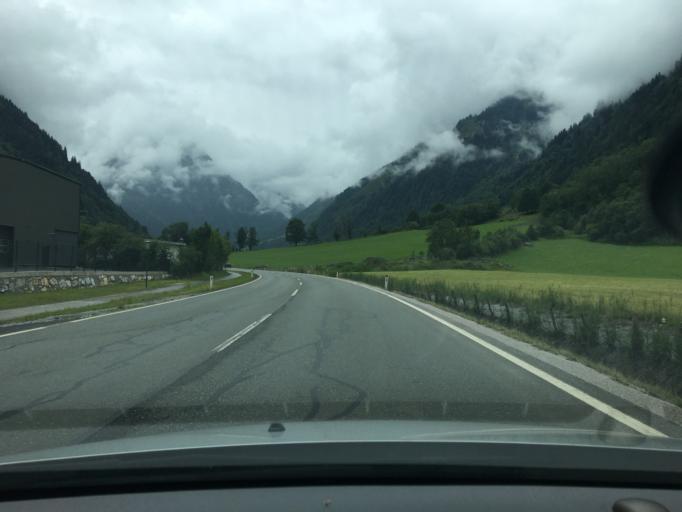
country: AT
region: Salzburg
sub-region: Politischer Bezirk Zell am See
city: Bruck an der Grossglocknerstrasse
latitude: 47.2396
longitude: 12.8244
